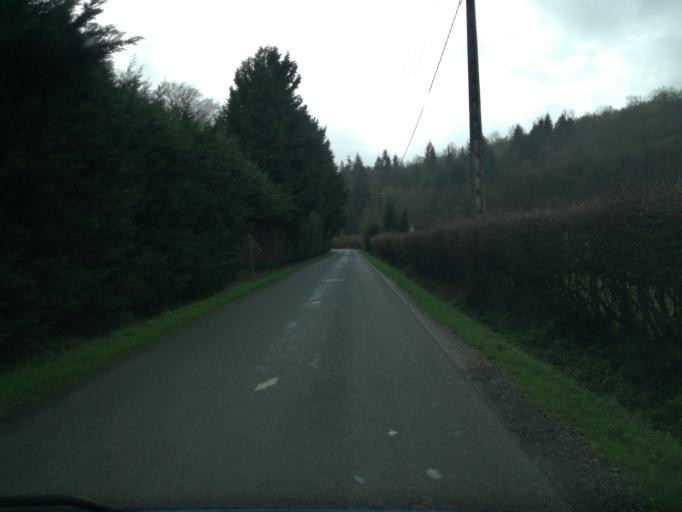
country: FR
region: Haute-Normandie
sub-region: Departement de la Seine-Maritime
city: Saint-Wandrille-Rancon
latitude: 49.5509
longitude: 0.7555
